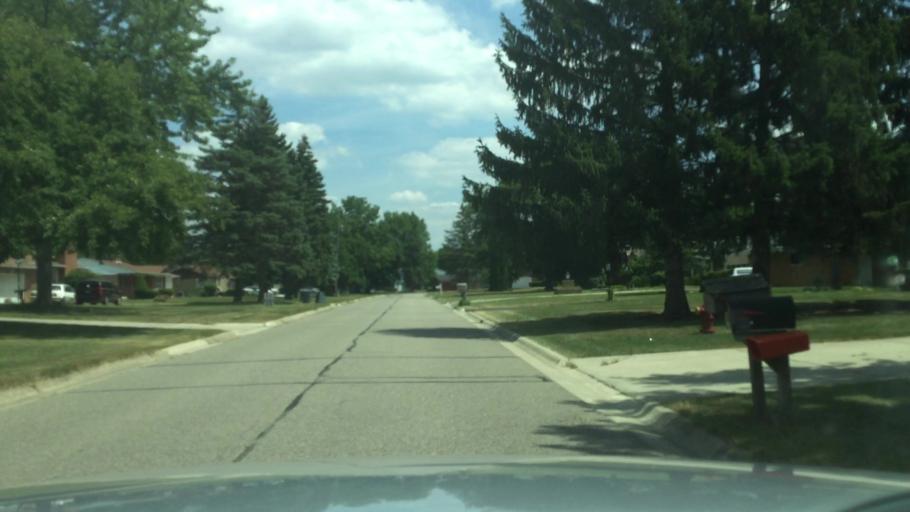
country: US
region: Michigan
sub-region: Genesee County
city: Grand Blanc
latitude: 42.9428
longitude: -83.6890
